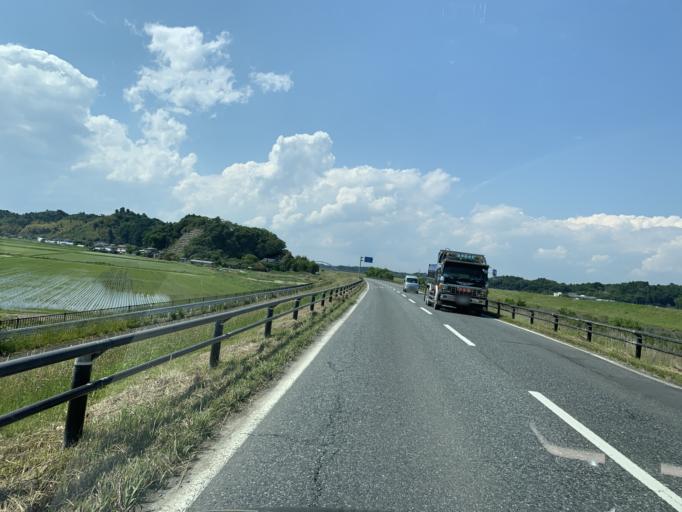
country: JP
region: Miyagi
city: Yamoto
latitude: 38.3988
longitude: 141.1545
